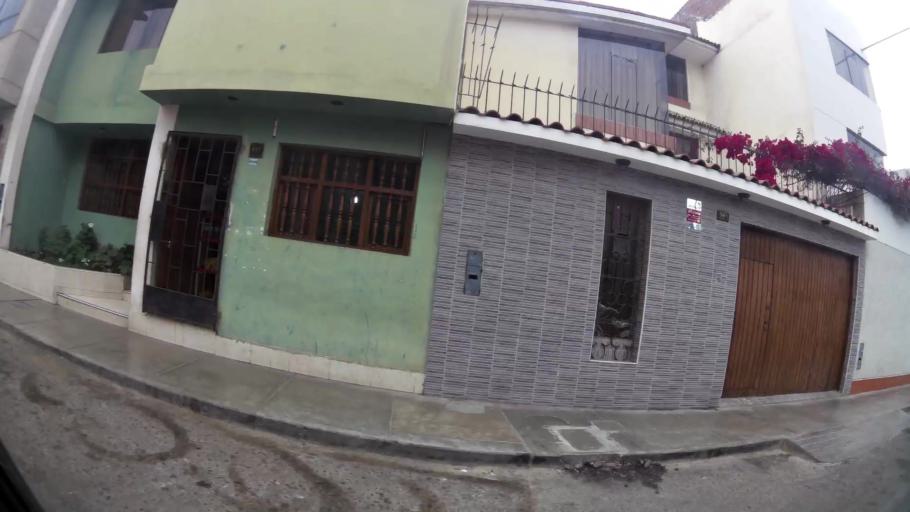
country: PE
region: La Libertad
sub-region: Provincia de Trujillo
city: Trujillo
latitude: -8.1221
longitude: -79.0293
